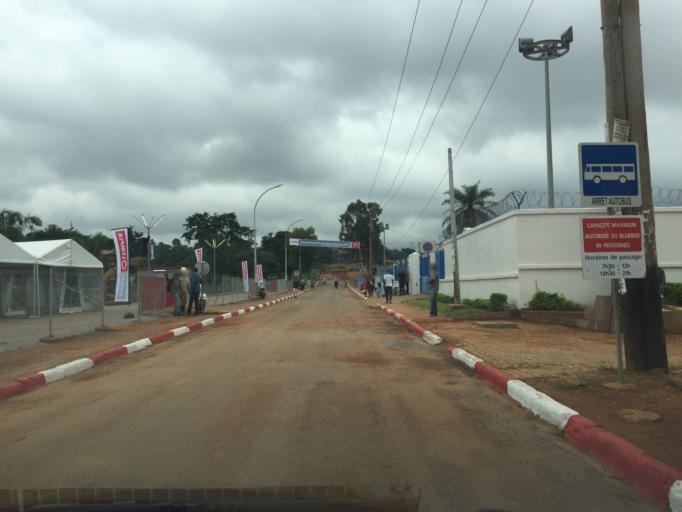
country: CM
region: Centre
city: Yaounde
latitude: 3.8591
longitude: 11.4964
